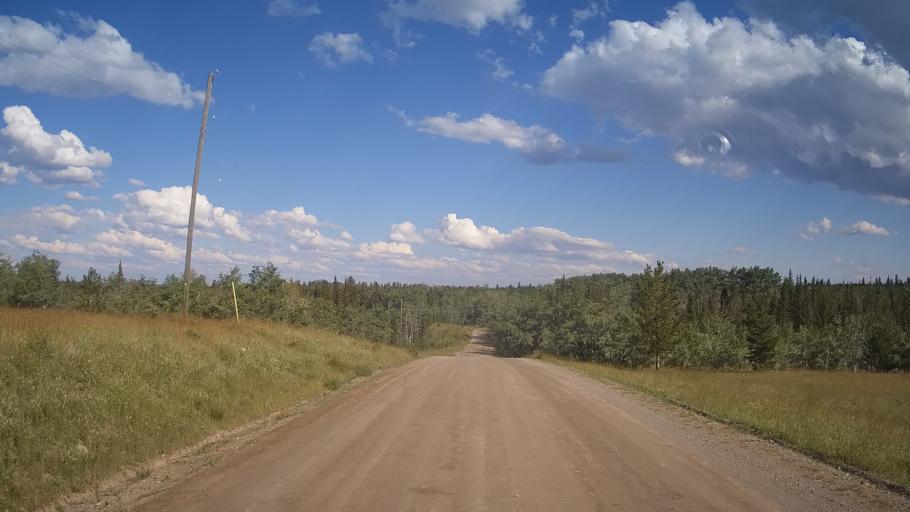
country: CA
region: British Columbia
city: Cache Creek
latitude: 51.2771
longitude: -121.7324
